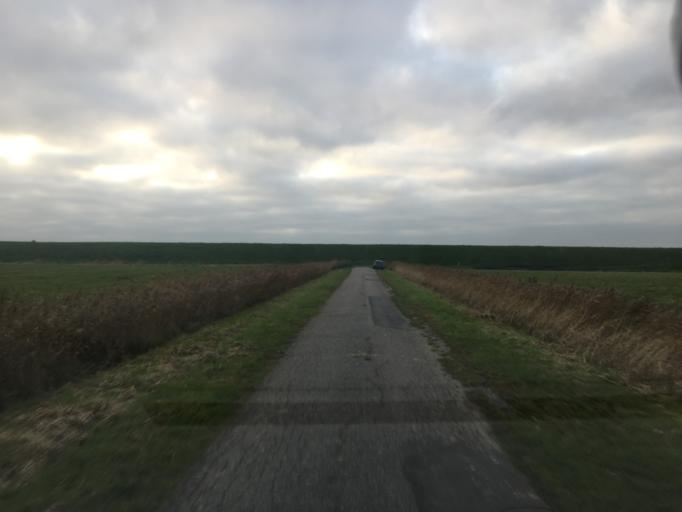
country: DE
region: Schleswig-Holstein
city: Klanxbull
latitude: 54.9273
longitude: 8.6710
